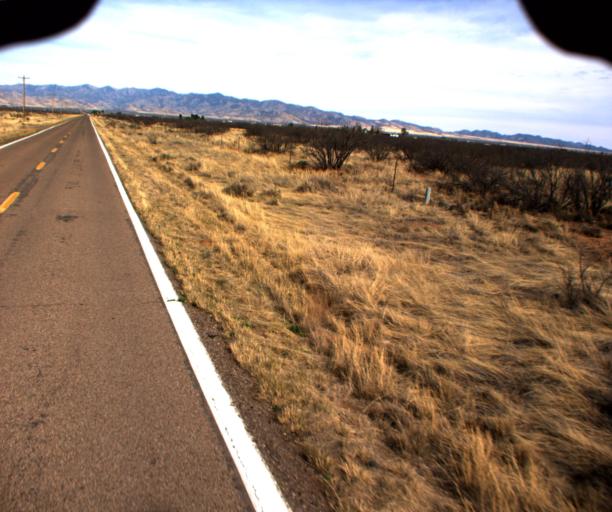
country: US
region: Arizona
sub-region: Cochise County
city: Willcox
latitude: 31.8762
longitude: -109.5925
